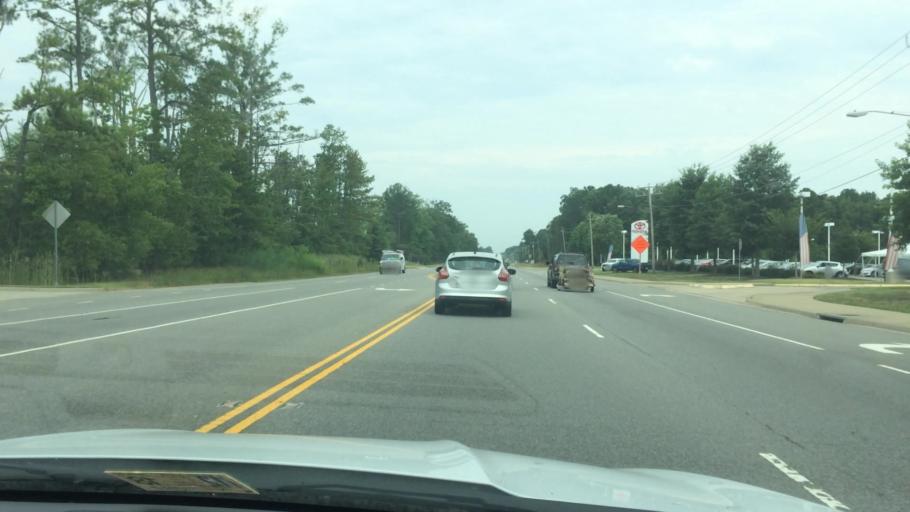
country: US
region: Virginia
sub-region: York County
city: Yorktown
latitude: 37.1576
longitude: -76.5349
